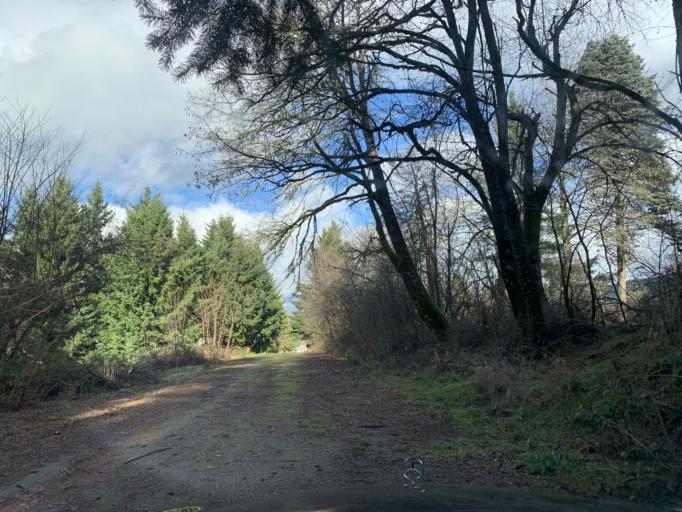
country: US
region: Washington
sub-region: Skamania County
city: Carson
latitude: 45.7235
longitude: -121.8172
